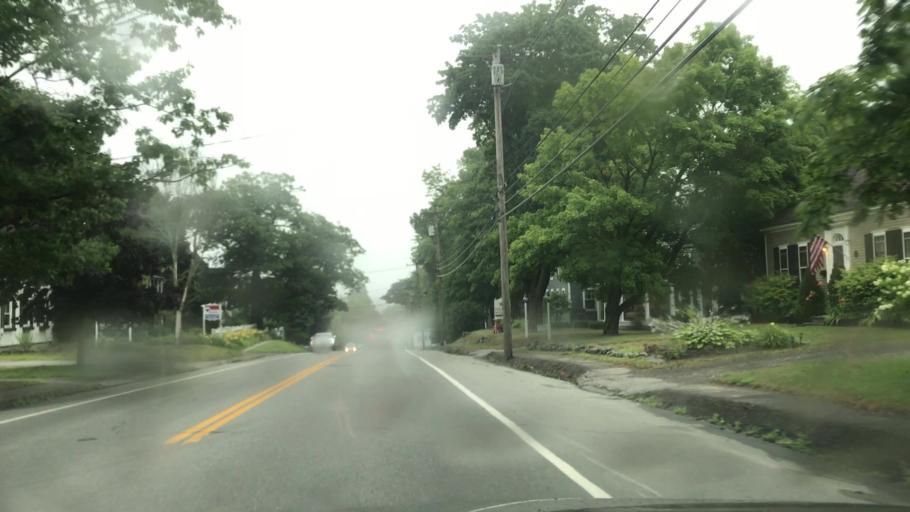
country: US
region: Maine
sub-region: Knox County
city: Camden
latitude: 44.2059
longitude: -69.0700
